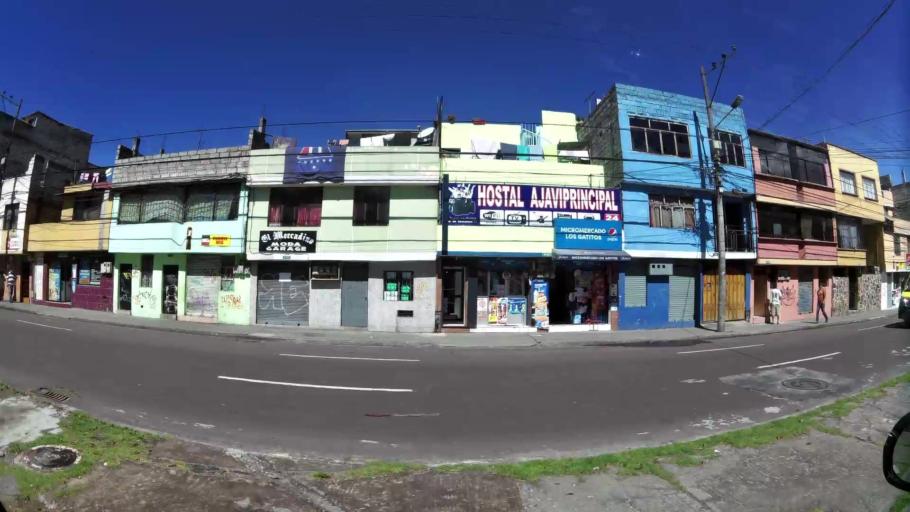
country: EC
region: Pichincha
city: Quito
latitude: -0.2673
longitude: -78.5340
